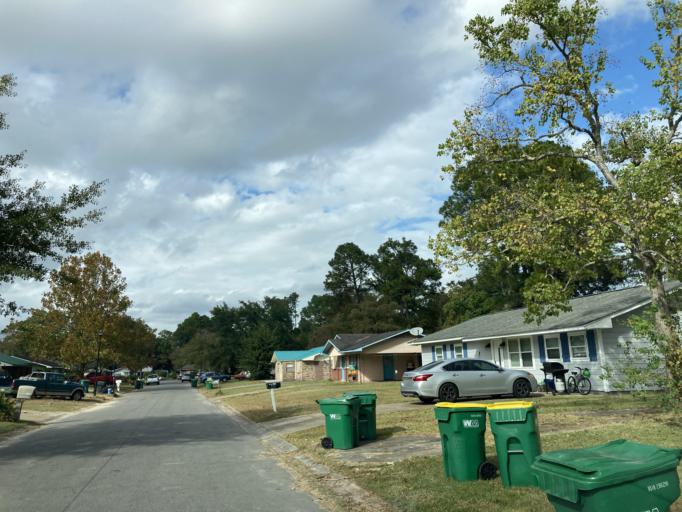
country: US
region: Mississippi
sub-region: Jackson County
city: Gulf Hills
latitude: 30.4363
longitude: -88.8245
